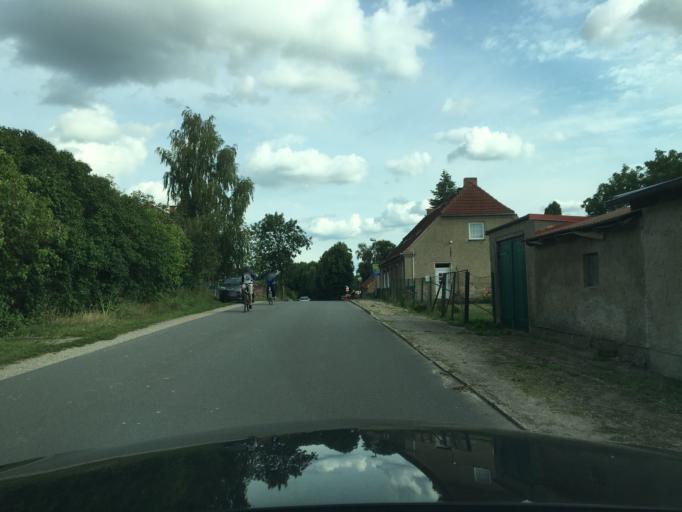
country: DE
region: Mecklenburg-Vorpommern
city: Mollenhagen
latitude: 53.4826
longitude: 12.9612
